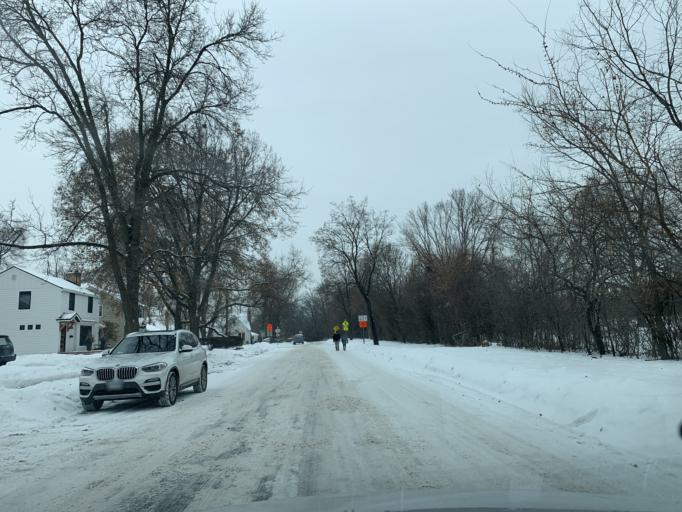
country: US
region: Minnesota
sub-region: Hennepin County
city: Saint Louis Park
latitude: 44.9428
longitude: -93.3291
